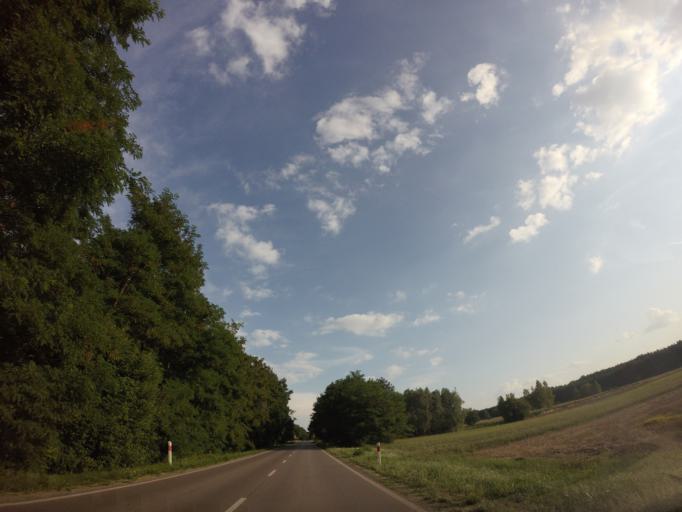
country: PL
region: Lublin Voivodeship
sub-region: Powiat lubartowski
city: Michow
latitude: 51.5604
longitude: 22.2977
